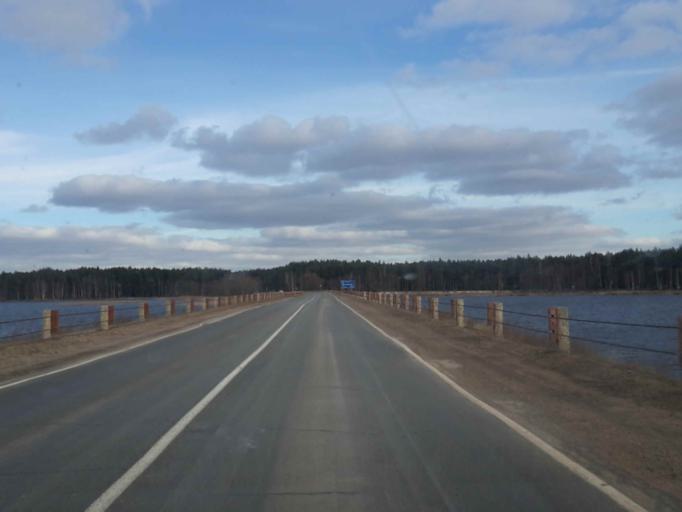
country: BY
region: Minsk
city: Il'ya
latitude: 54.5026
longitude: 27.2350
